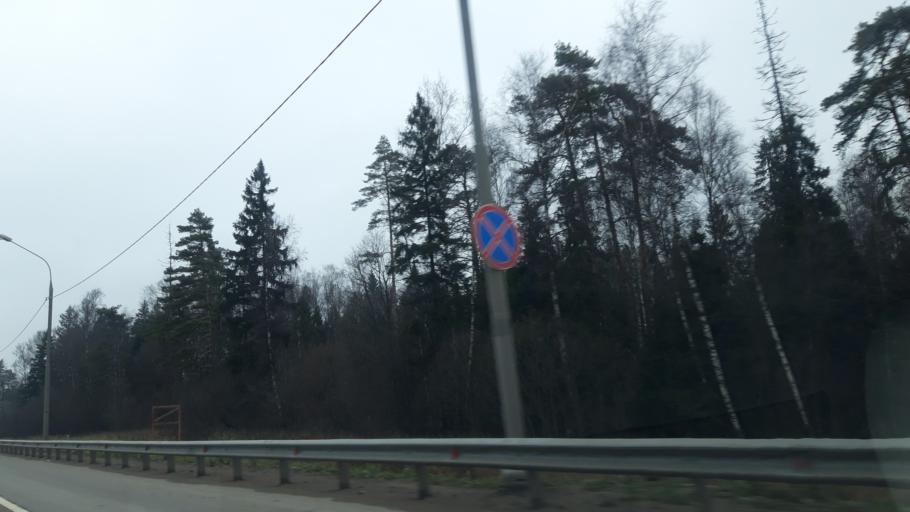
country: RU
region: Moskovskaya
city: Lozhki
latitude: 56.0809
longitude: 37.1223
